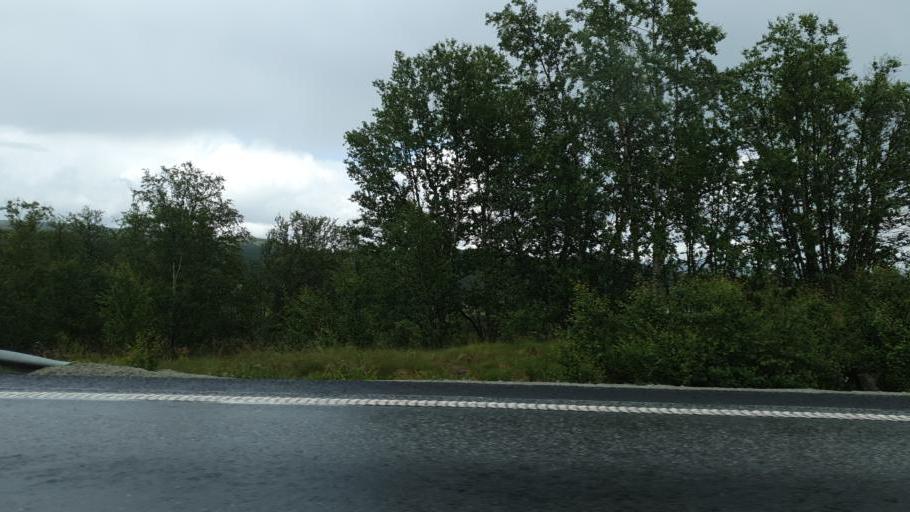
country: NO
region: Oppland
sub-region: Dovre
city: Dovre
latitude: 62.2120
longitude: 9.5592
